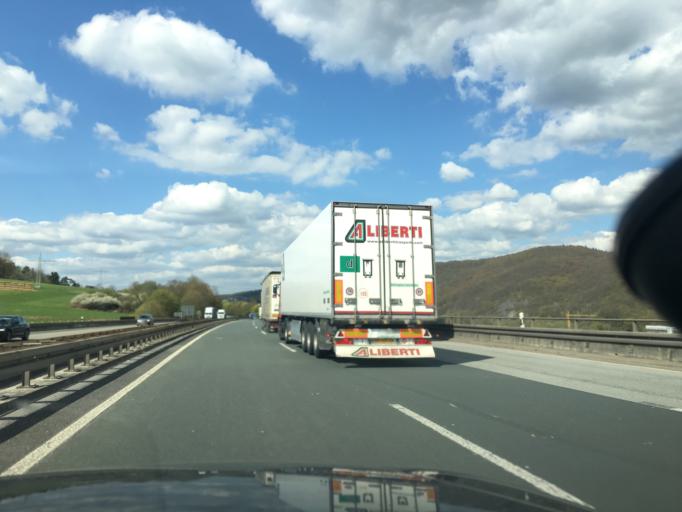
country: DE
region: Hesse
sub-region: Regierungsbezirk Giessen
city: Sinn
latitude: 50.6529
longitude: 8.3208
